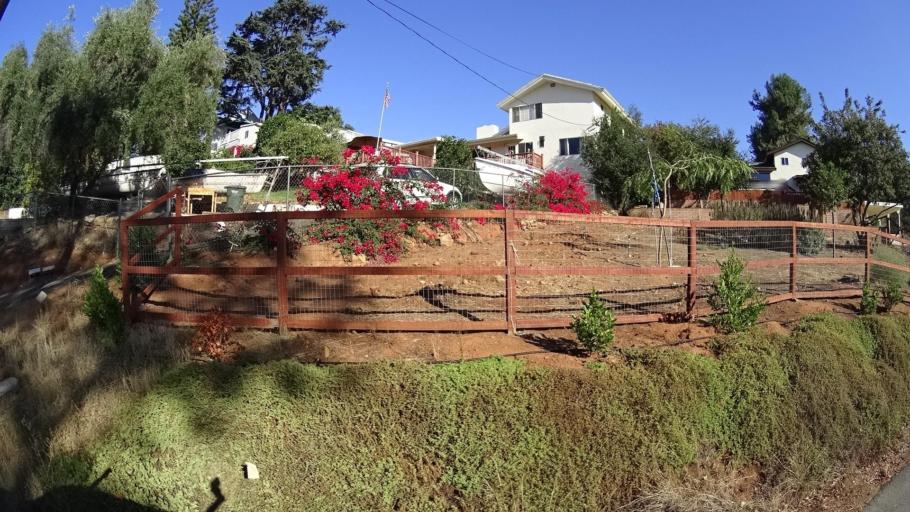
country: US
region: California
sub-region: San Diego County
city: Casa de Oro-Mount Helix
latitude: 32.7726
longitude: -116.9946
